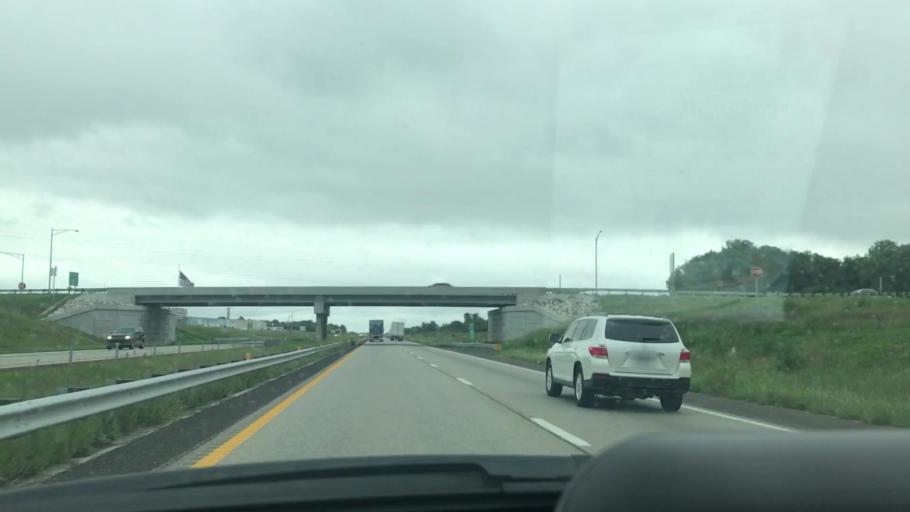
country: US
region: Missouri
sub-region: Greene County
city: Republic
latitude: 37.2003
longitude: -93.4243
